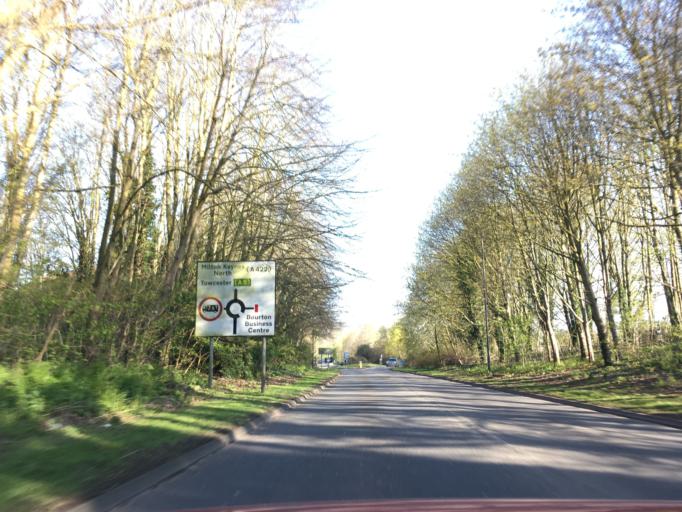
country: GB
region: England
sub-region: Buckinghamshire
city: Buckingham
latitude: 51.9931
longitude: -0.9684
